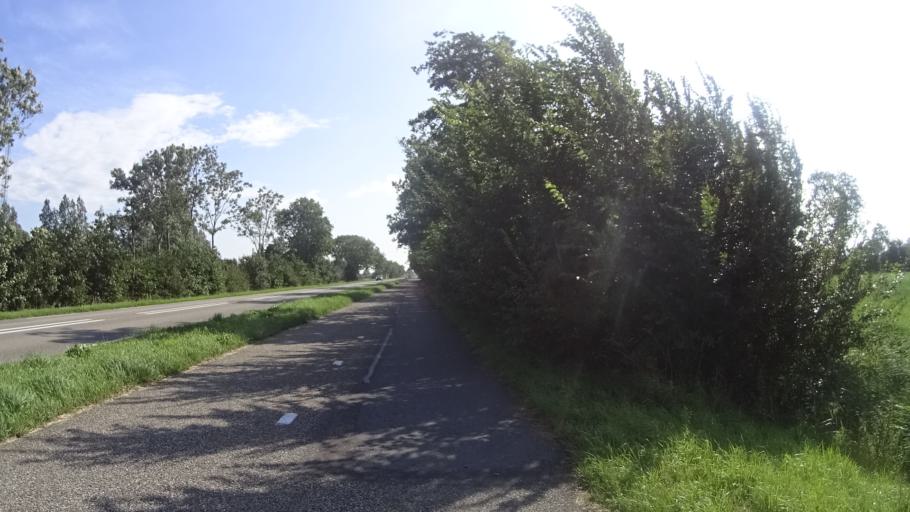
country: NL
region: Friesland
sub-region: Menameradiel
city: Dronryp
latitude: 53.1956
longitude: 5.6159
